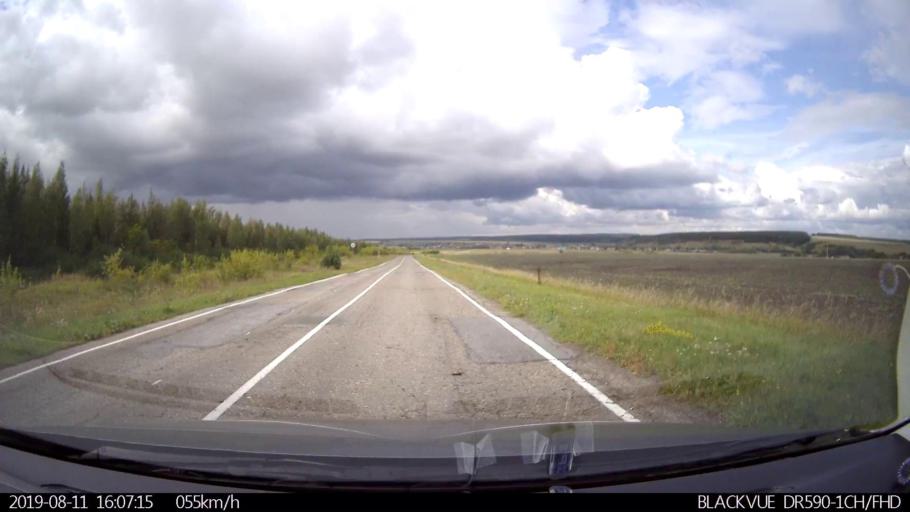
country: RU
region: Ulyanovsk
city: Ignatovka
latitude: 53.9748
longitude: 47.6511
